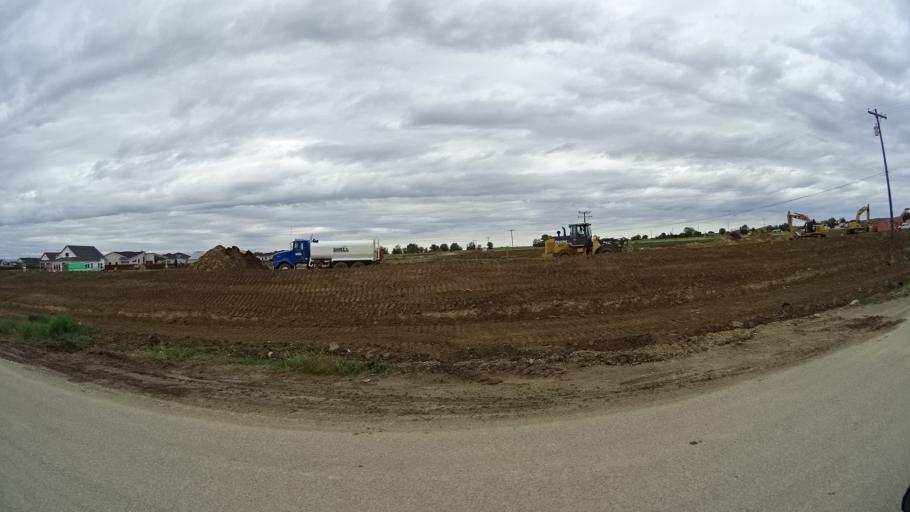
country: US
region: Idaho
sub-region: Ada County
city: Eagle
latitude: 43.7168
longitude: -116.4234
